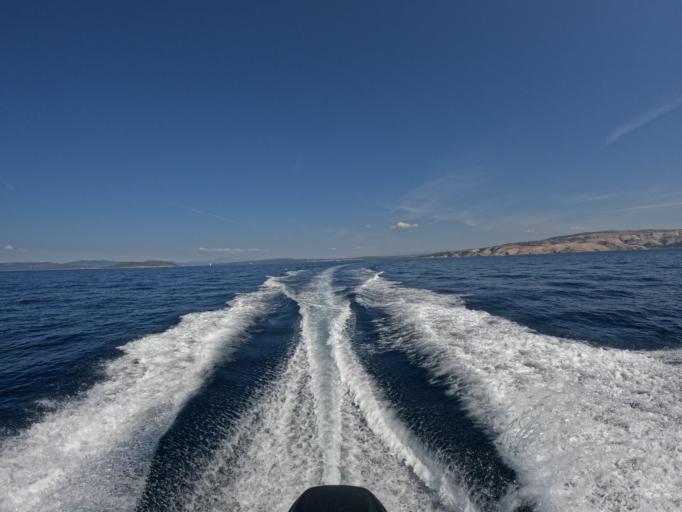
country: HR
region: Primorsko-Goranska
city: Punat
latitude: 44.9217
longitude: 14.6212
